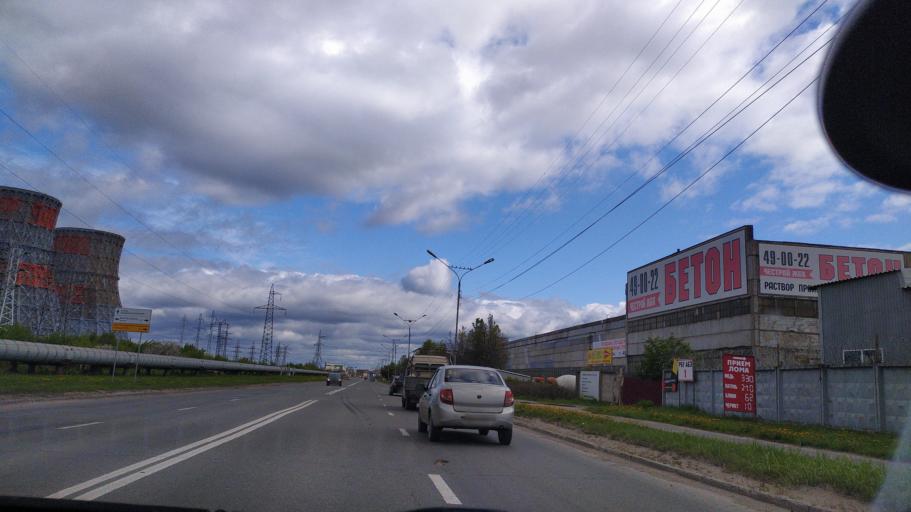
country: RU
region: Chuvashia
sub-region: Cheboksarskiy Rayon
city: Cheboksary
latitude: 56.1222
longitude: 47.3045
